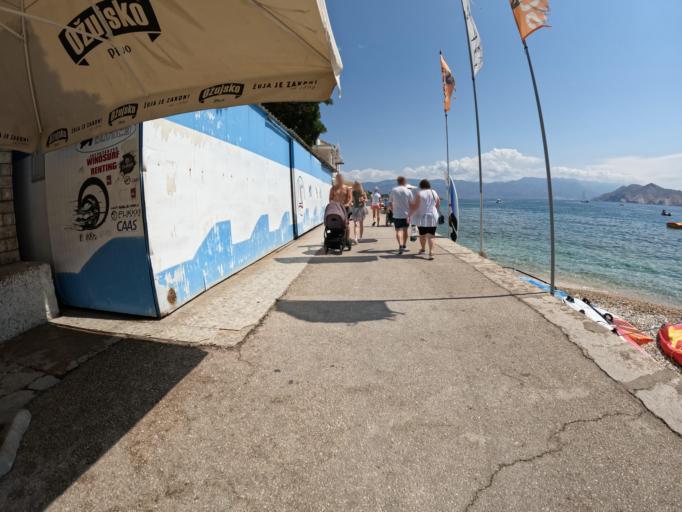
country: HR
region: Primorsko-Goranska
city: Punat
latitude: 44.9695
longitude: 14.7546
